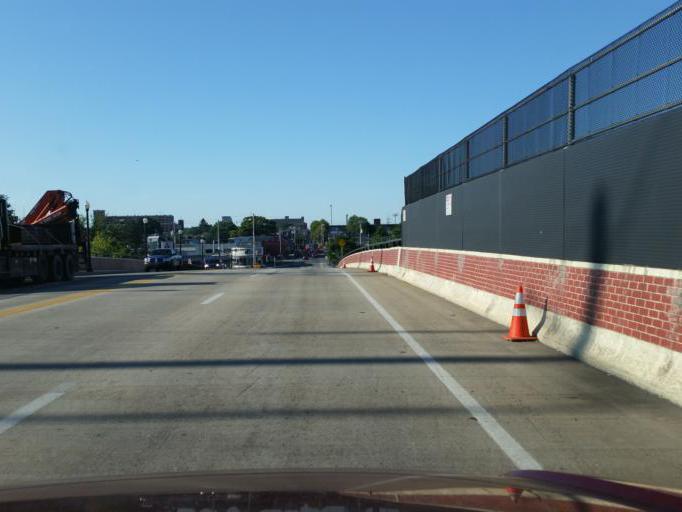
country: US
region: Pennsylvania
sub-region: Lancaster County
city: Lancaster
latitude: 40.0554
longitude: -76.3109
